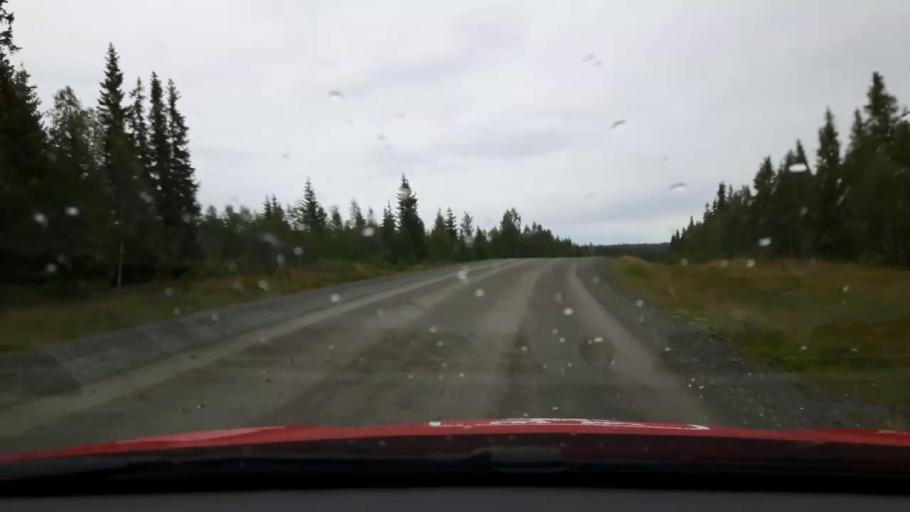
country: SE
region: Jaemtland
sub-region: Are Kommun
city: Are
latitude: 63.4692
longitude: 12.6052
